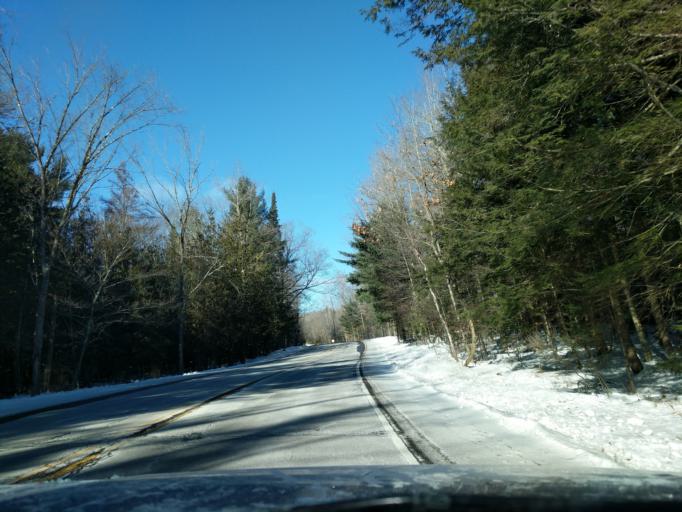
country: US
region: Wisconsin
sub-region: Menominee County
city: Keshena
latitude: 45.1084
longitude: -88.6394
